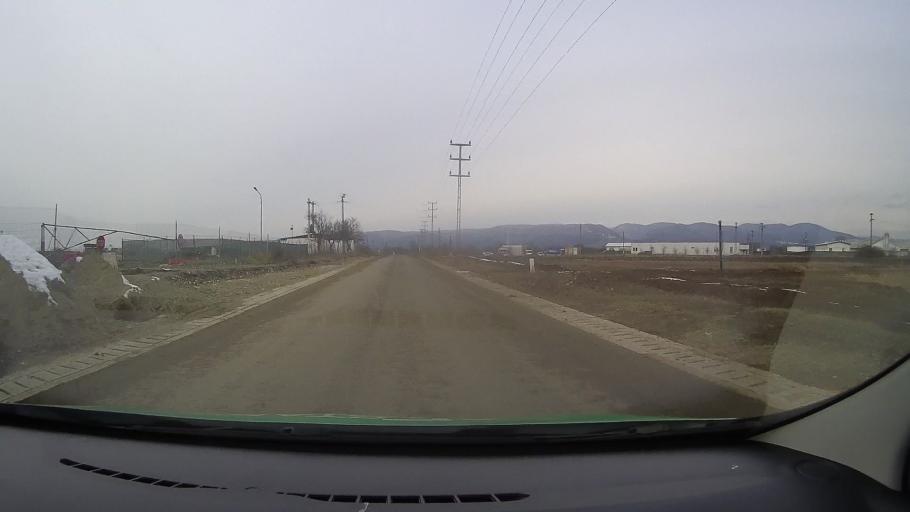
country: RO
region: Hunedoara
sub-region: Comuna Turdas
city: Turdas
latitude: 45.8430
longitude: 23.1374
